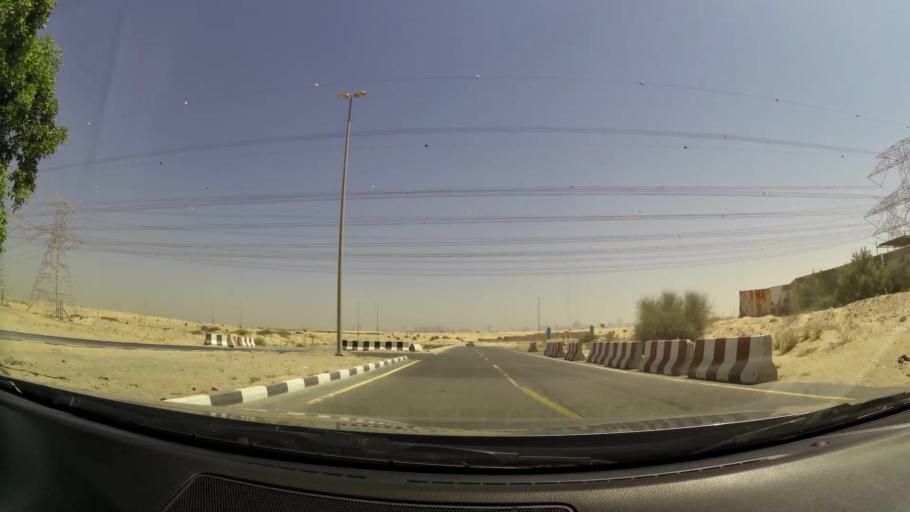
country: AE
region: Dubai
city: Dubai
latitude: 24.9907
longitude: 55.2005
